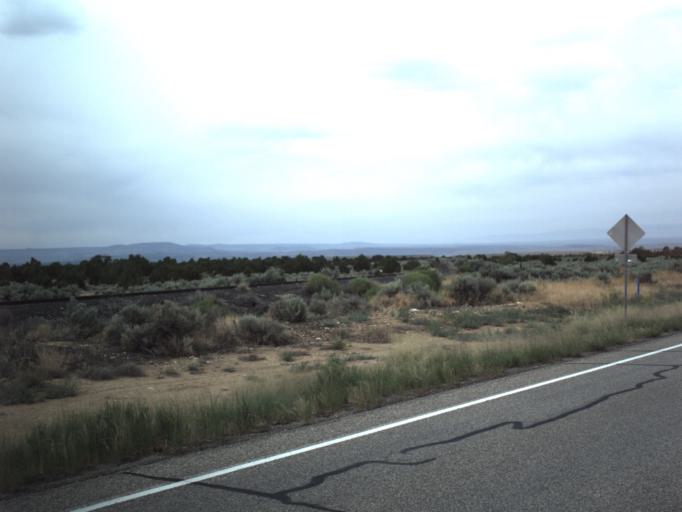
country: US
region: Utah
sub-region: Carbon County
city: East Carbon City
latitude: 39.5406
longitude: -110.4300
